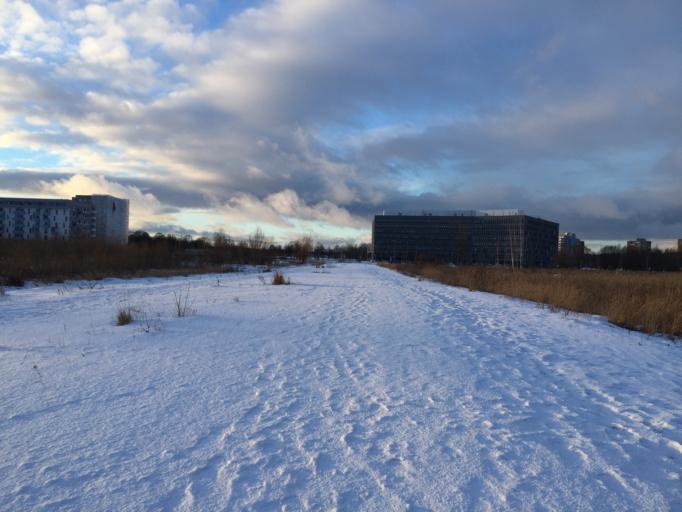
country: LV
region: Riga
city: Jaunciems
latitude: 56.9894
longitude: 24.1759
